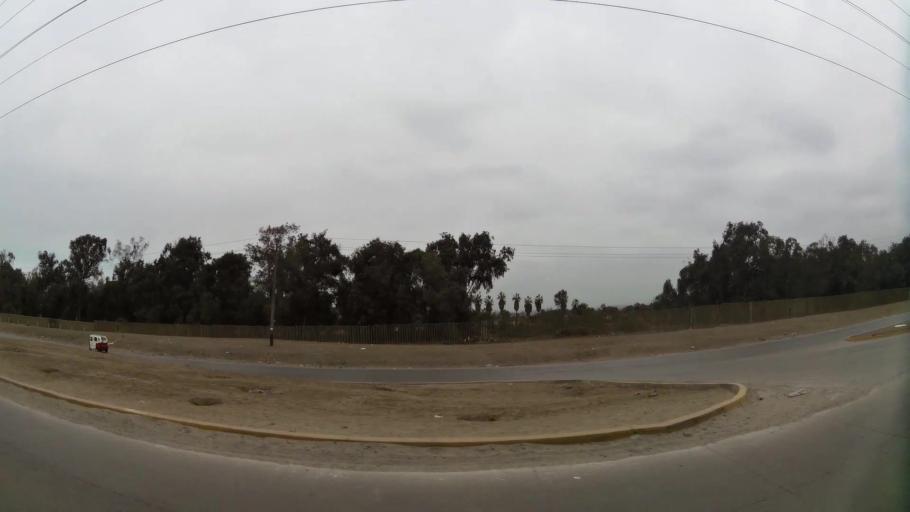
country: PE
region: Lima
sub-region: Lima
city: Surco
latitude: -12.2081
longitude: -76.9569
